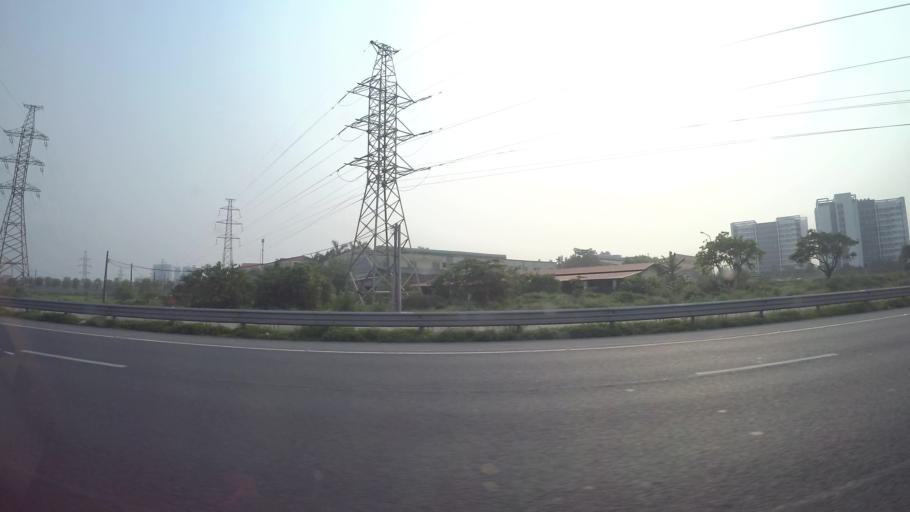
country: VN
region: Ha Noi
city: Van Dien
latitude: 20.9479
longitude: 105.8565
